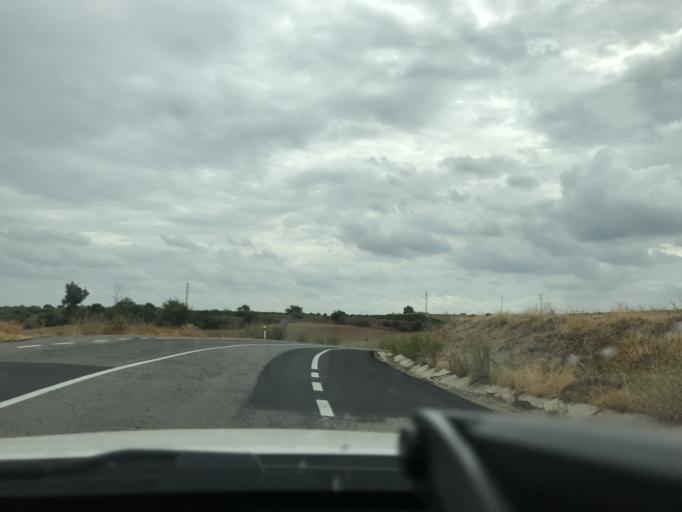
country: ES
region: Andalusia
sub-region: Provincia de Sevilla
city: Cantillana
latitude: 37.6202
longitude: -5.7914
